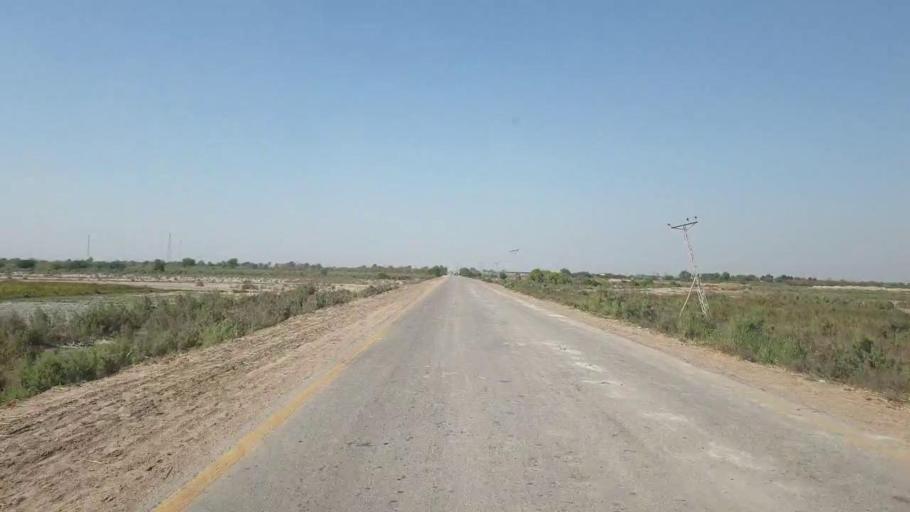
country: PK
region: Sindh
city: Rajo Khanani
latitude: 25.0545
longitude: 68.8050
